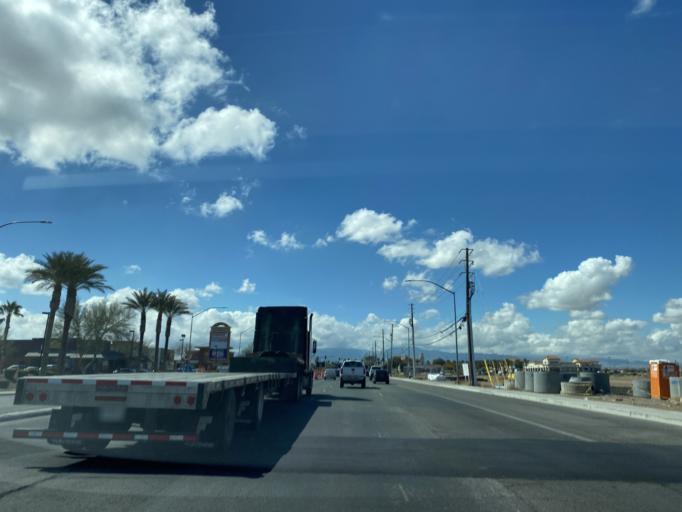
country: US
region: Nevada
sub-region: Clark County
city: North Las Vegas
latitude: 36.2395
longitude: -115.1543
